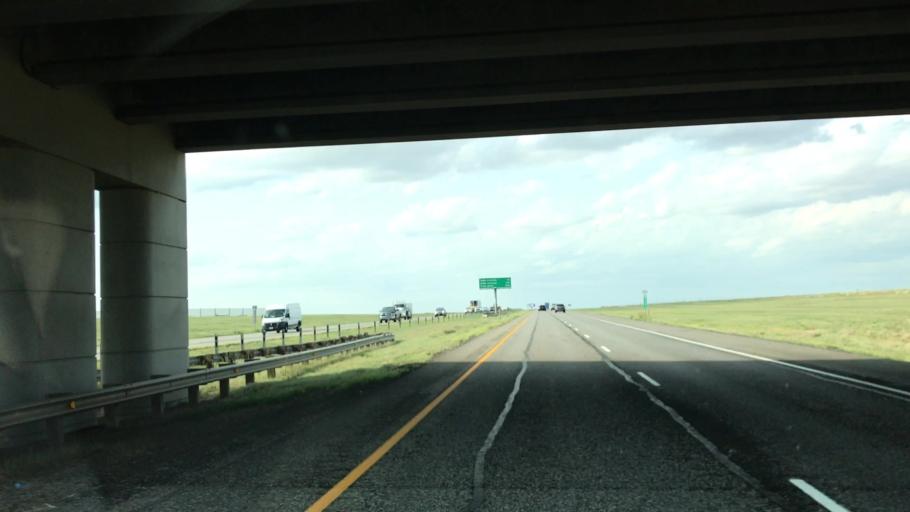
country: US
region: Colorado
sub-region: Adams County
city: Aurora
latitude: 39.7837
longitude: -104.7163
